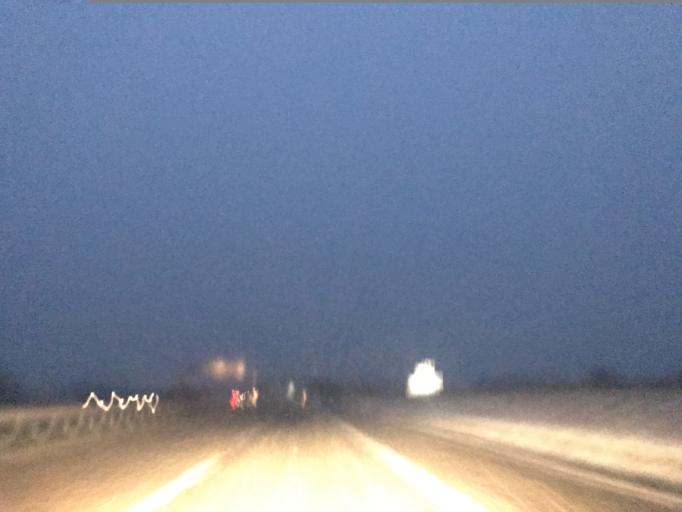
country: FR
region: Auvergne
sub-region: Departement du Puy-de-Dome
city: Charbonnieres-les-Varennes
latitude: 45.9593
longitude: 3.0153
